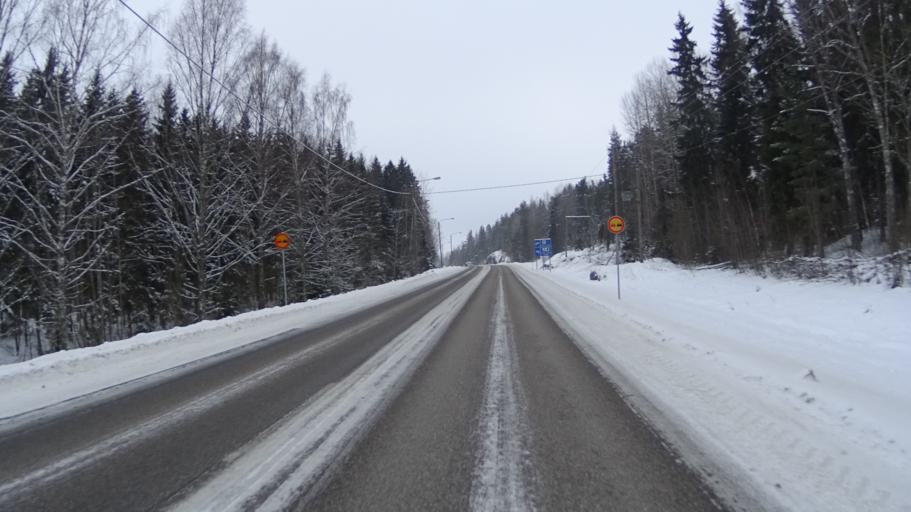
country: FI
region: Uusimaa
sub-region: Helsinki
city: Vihti
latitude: 60.3580
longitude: 24.1777
